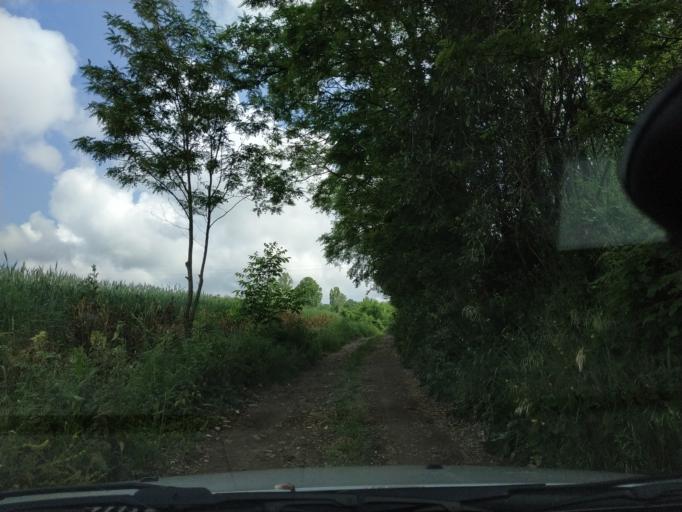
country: RS
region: Central Serbia
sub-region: Nisavski Okrug
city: Aleksinac
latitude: 43.4267
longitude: 21.5882
